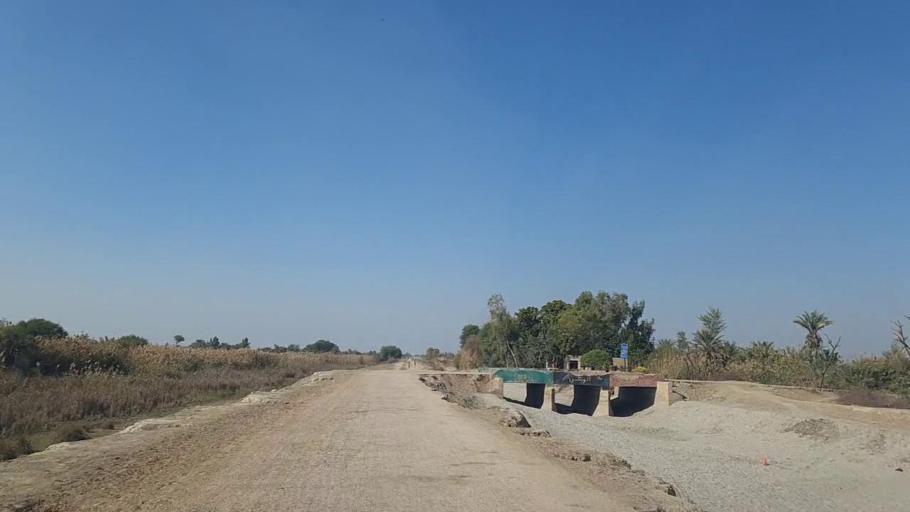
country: PK
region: Sindh
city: Jam Sahib
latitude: 26.2222
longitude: 68.6019
